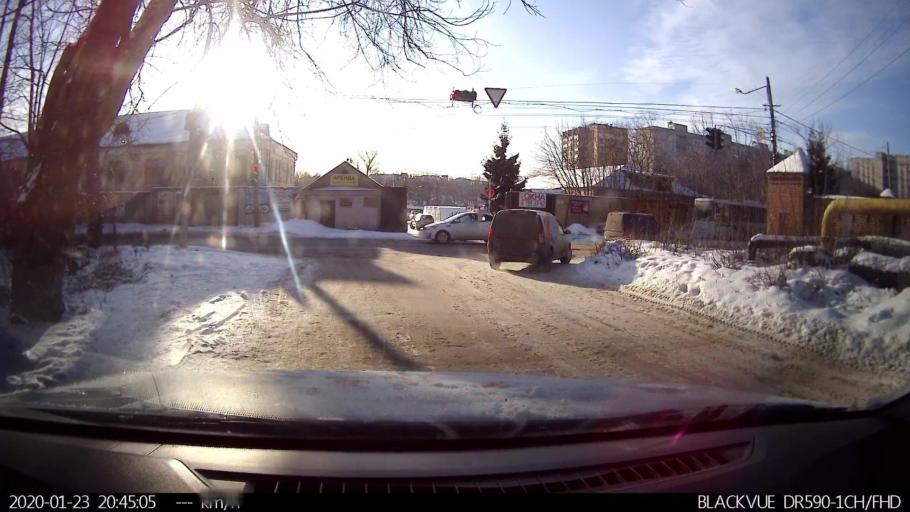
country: RU
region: Nizjnij Novgorod
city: Nizhniy Novgorod
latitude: 56.2987
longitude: 43.9972
